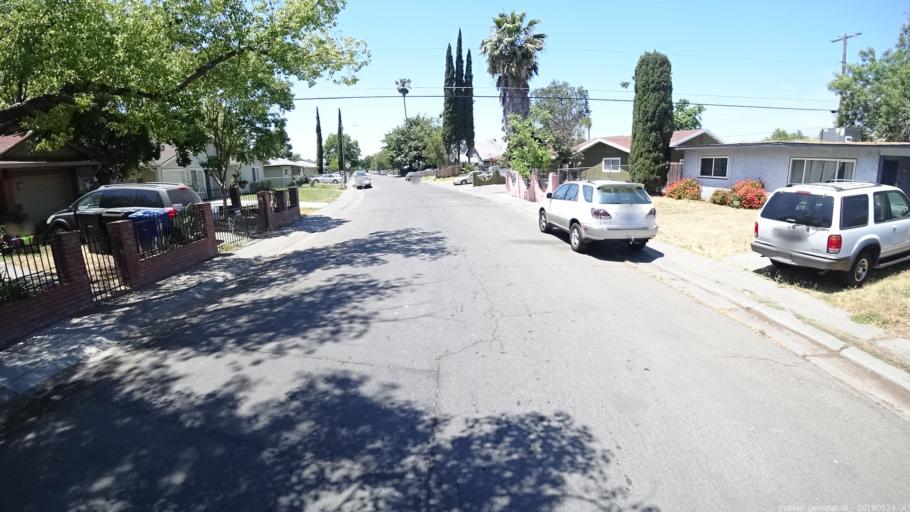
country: US
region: California
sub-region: Sacramento County
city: Sacramento
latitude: 38.6228
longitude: -121.4598
